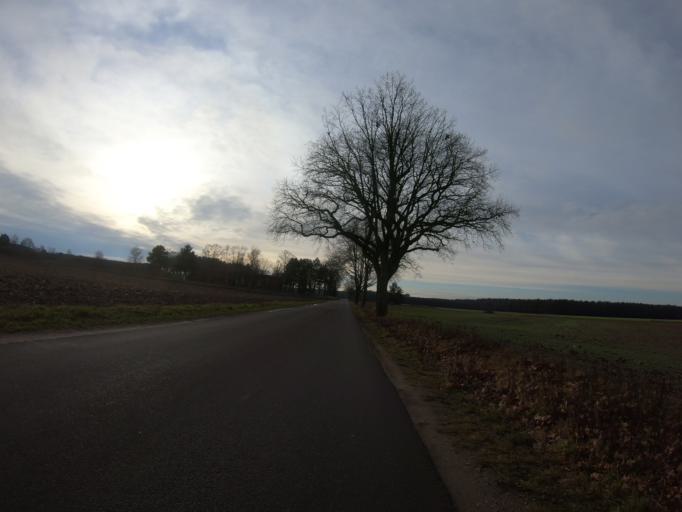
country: DE
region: Lower Saxony
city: Muden
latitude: 52.4968
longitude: 10.4053
